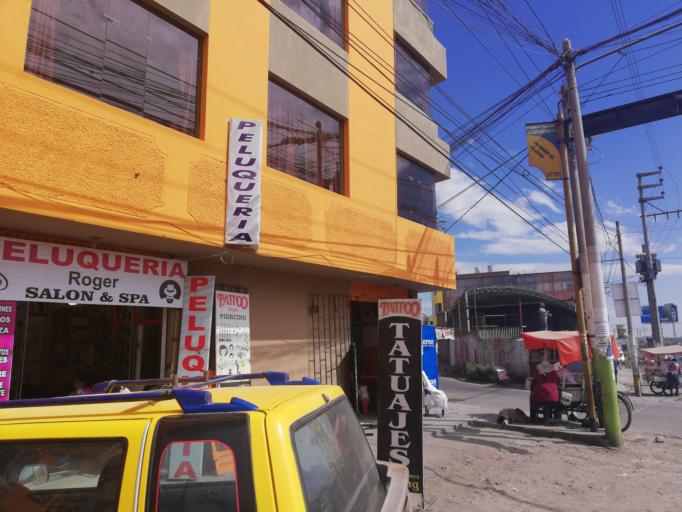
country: PE
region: Arequipa
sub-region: Provincia de Arequipa
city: Arequipa
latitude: -16.4232
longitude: -71.5414
